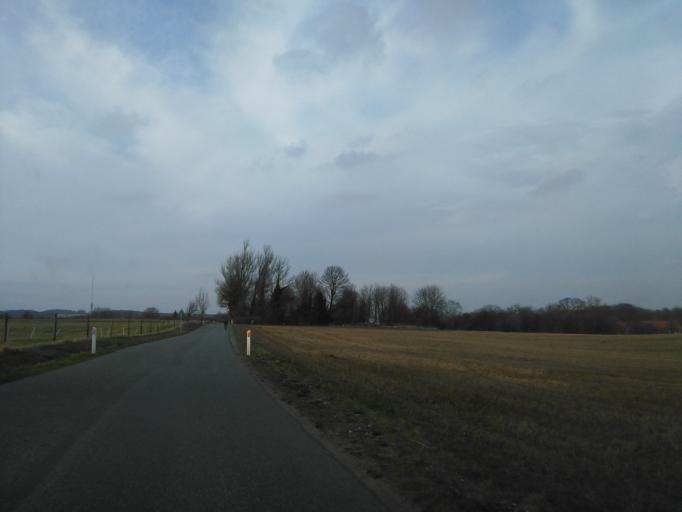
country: DK
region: Central Jutland
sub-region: Arhus Kommune
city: Beder
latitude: 56.0742
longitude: 10.2359
